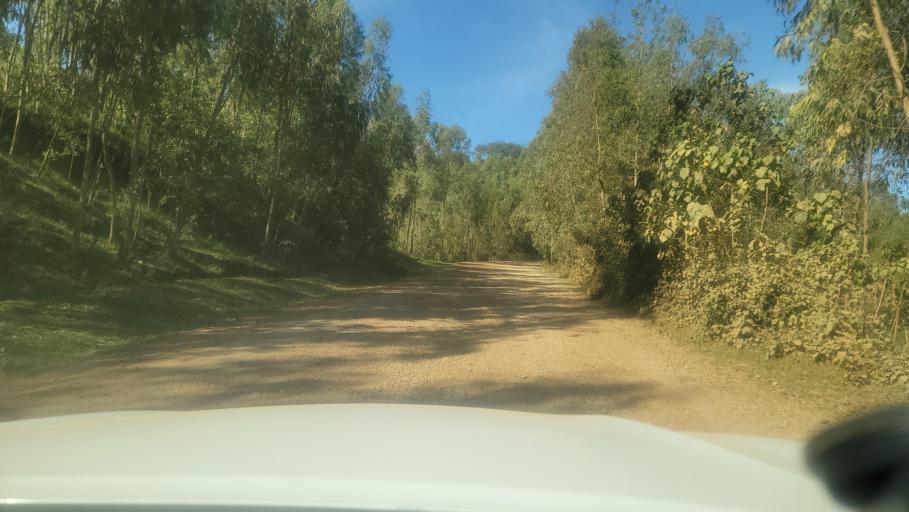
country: ET
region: Oromiya
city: Agaro
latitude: 7.8004
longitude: 36.4683
